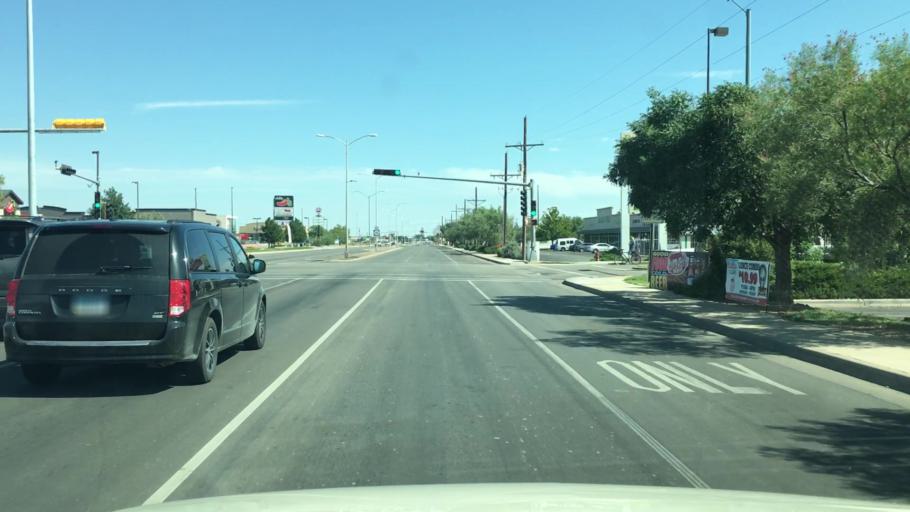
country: US
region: New Mexico
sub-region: Chaves County
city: Roswell
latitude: 33.4483
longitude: -104.5233
